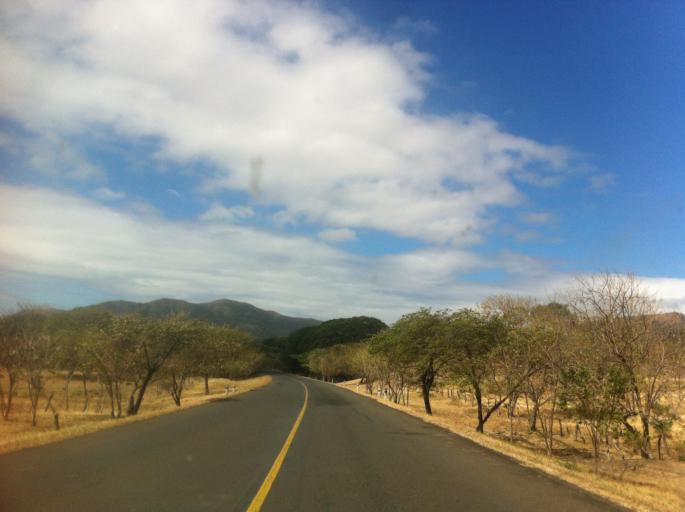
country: NI
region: Chontales
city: Acoyapa
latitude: 12.0039
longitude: -85.1790
